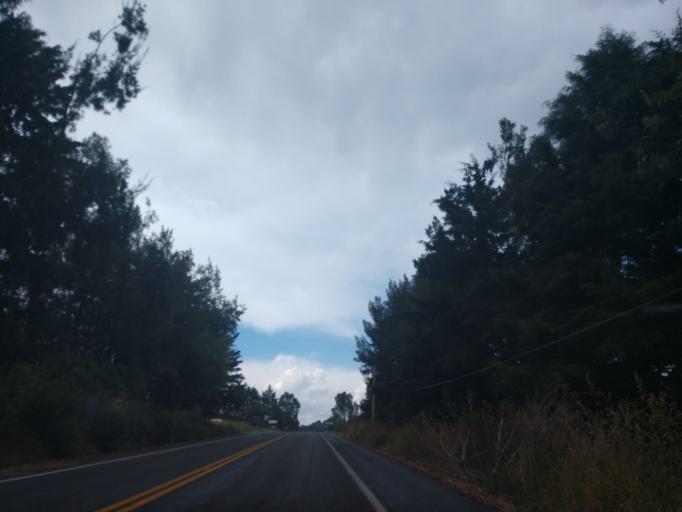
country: MX
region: Jalisco
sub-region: Mazamitla
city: Mazamitla
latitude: 19.9387
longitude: -103.0581
